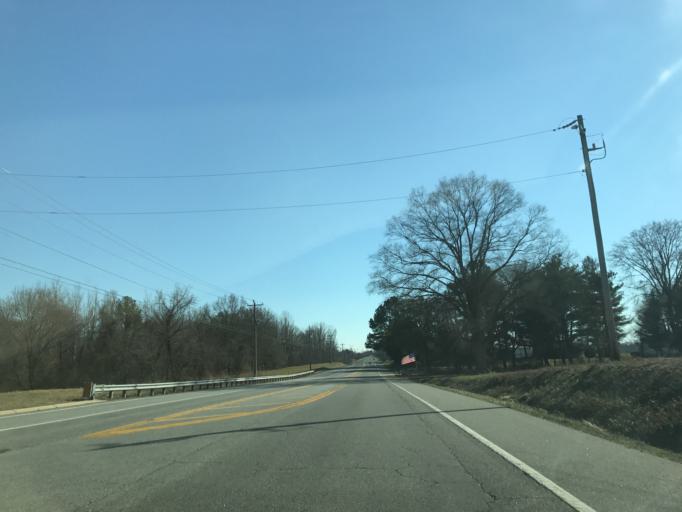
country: US
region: Maryland
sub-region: Queen Anne's County
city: Centreville
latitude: 39.0235
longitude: -76.0770
